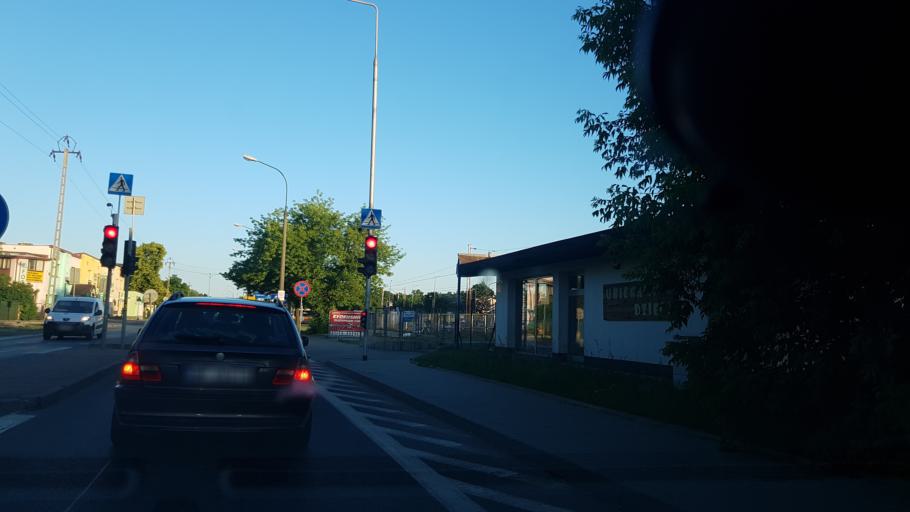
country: PL
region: Masovian Voivodeship
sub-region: Warszawa
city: Wawer
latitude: 52.1854
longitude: 21.1880
